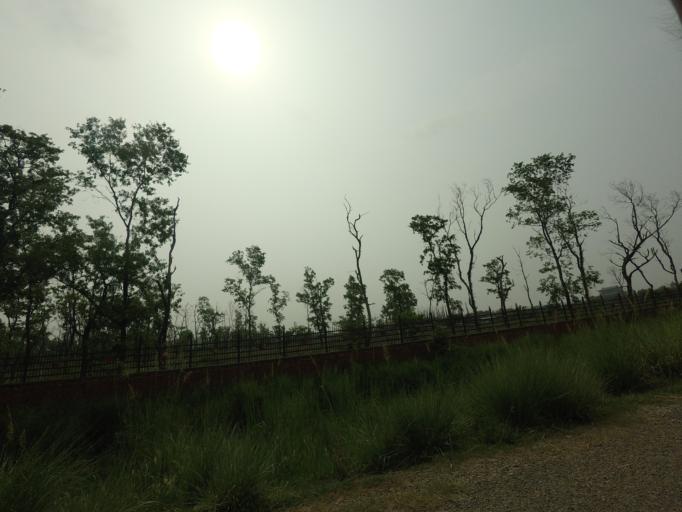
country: IN
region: Uttar Pradesh
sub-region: Maharajganj
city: Nautanwa
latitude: 27.4841
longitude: 83.2680
